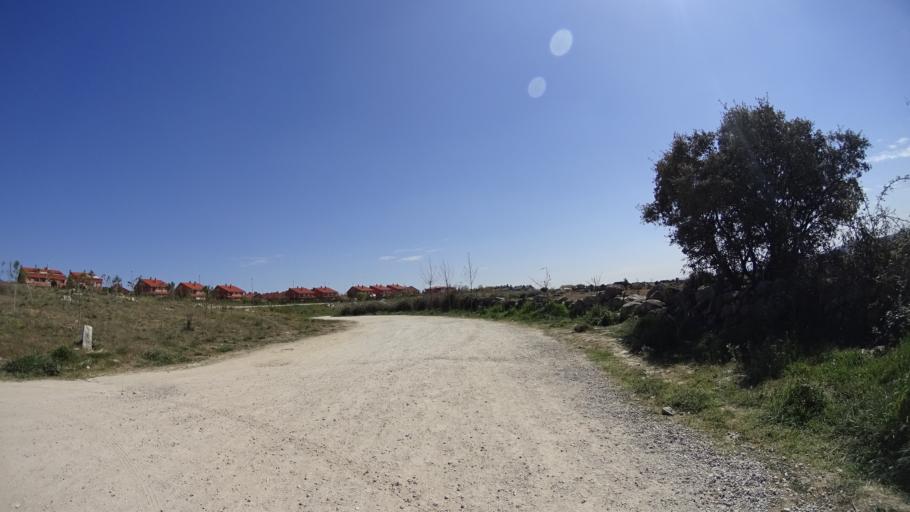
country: ES
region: Madrid
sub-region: Provincia de Madrid
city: Colmenar Viejo
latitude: 40.6699
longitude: -3.7861
